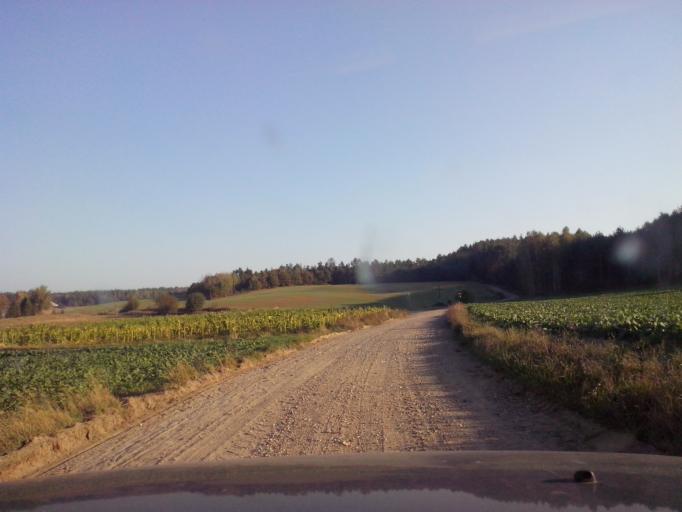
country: PL
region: Kujawsko-Pomorskie
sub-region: Powiat brodnicki
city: Gorzno
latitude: 53.2793
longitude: 19.7022
